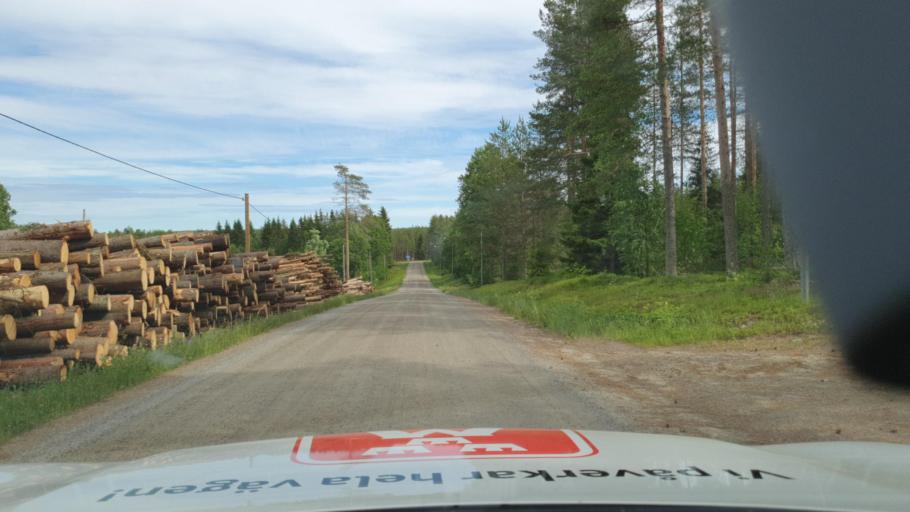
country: SE
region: Vaesterbotten
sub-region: Skelleftea Kommun
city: Burea
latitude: 64.3715
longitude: 21.0785
